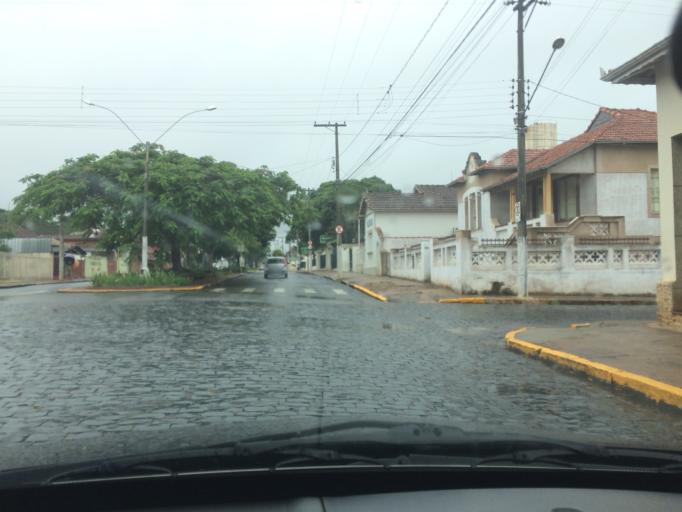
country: BR
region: Sao Paulo
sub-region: Casa Branca
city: Casa Branca
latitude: -21.7753
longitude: -47.0861
